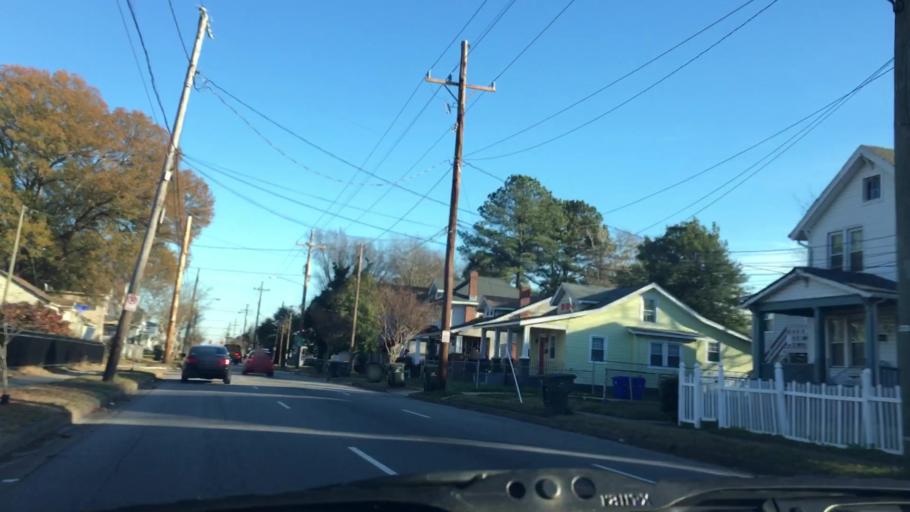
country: US
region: Virginia
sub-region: City of Norfolk
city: Norfolk
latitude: 36.8738
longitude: -76.2933
